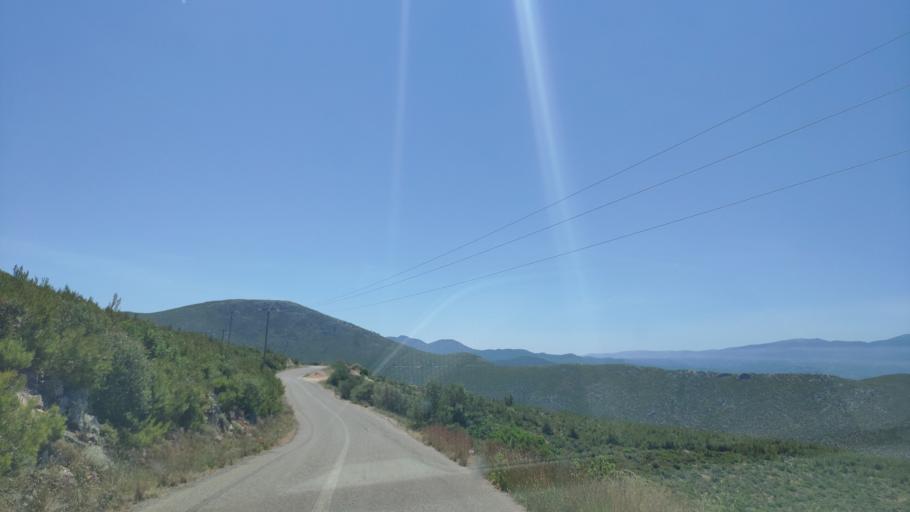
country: GR
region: Central Greece
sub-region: Nomos Voiotias
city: Kaparellion
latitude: 38.1954
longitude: 23.1467
